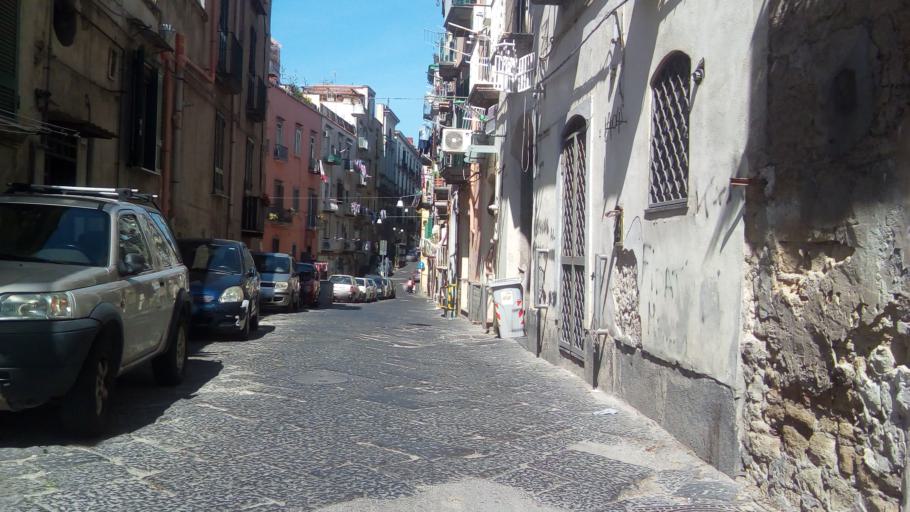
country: IT
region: Campania
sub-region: Provincia di Napoli
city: Napoli
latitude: 40.8648
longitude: 14.2543
